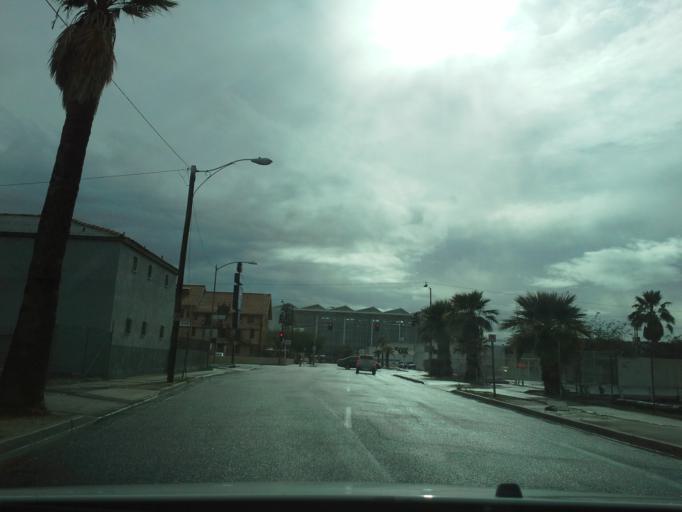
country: US
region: Arizona
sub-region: Maricopa County
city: Phoenix
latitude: 33.4522
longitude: -112.0802
